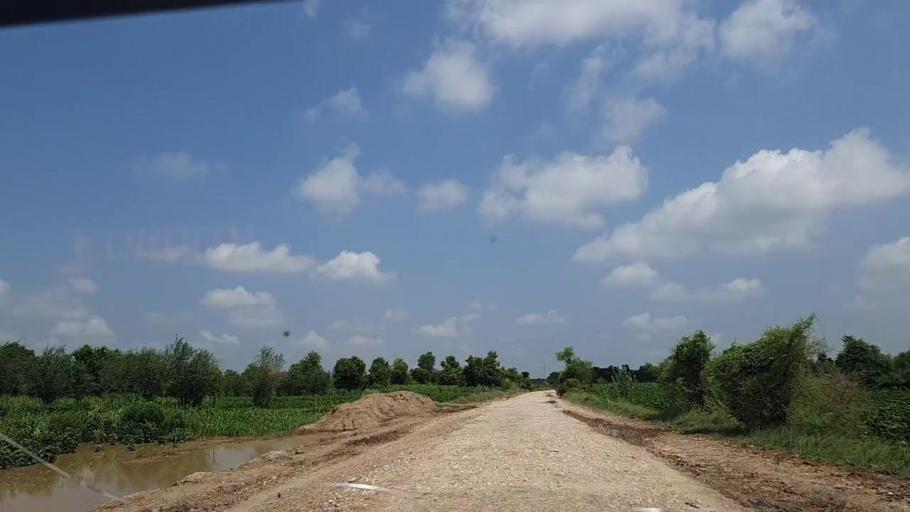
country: PK
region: Sindh
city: Tharu Shah
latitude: 26.8939
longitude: 68.0406
